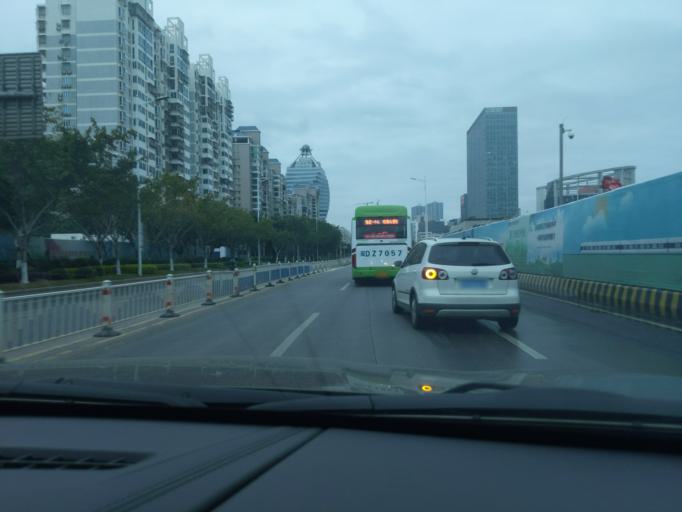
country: CN
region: Fujian
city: Liuwudian
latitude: 24.4835
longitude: 118.1802
